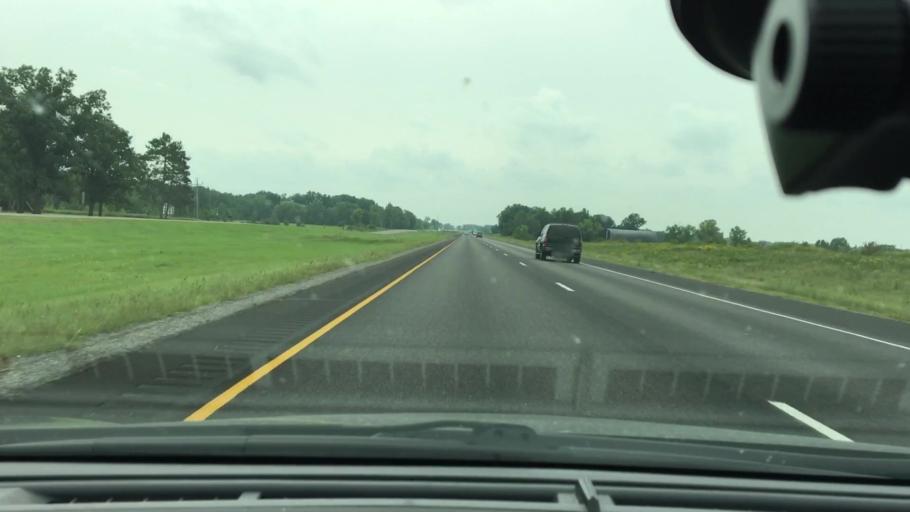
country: US
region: Minnesota
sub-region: Mille Lacs County
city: Milaca
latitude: 45.8063
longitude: -93.6550
